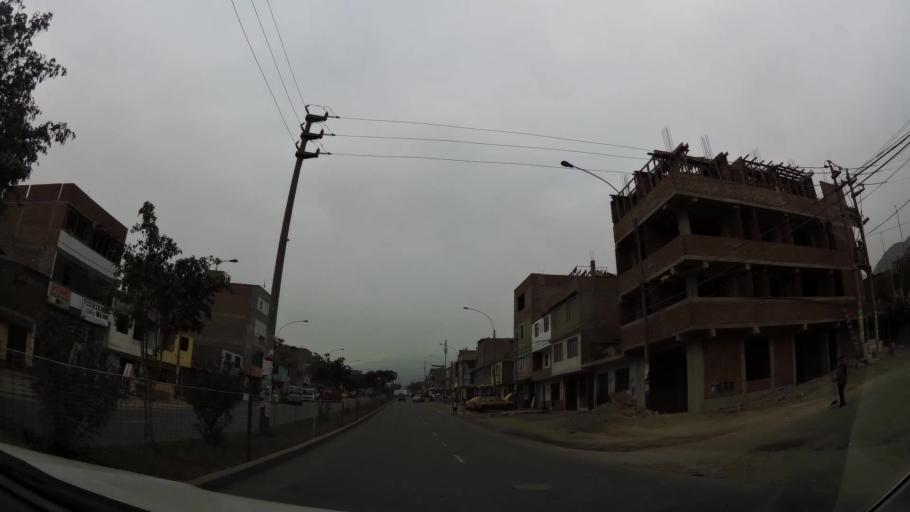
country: PE
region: Lima
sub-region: Lima
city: Independencia
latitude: -11.9638
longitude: -77.0083
